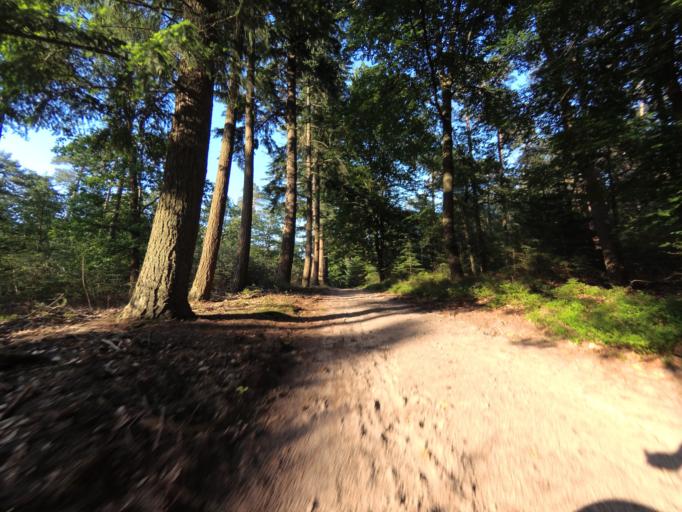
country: NL
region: Gelderland
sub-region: Gemeente Apeldoorn
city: Beekbergen
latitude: 52.1531
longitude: 5.9219
